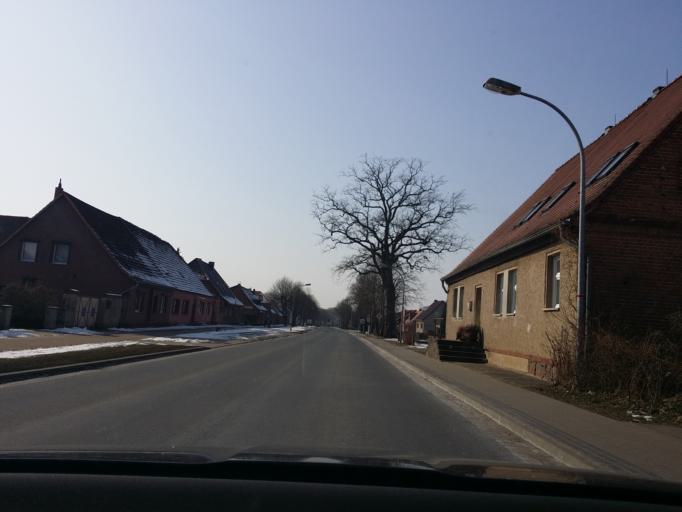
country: DE
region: Brandenburg
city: Heiligengrabe
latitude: 53.1451
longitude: 12.3640
